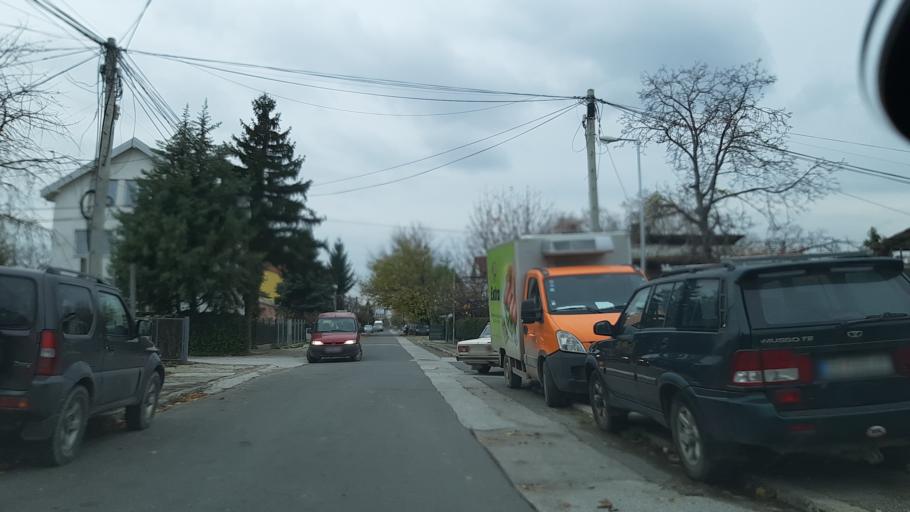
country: MK
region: Kisela Voda
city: Usje
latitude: 41.9715
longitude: 21.4733
